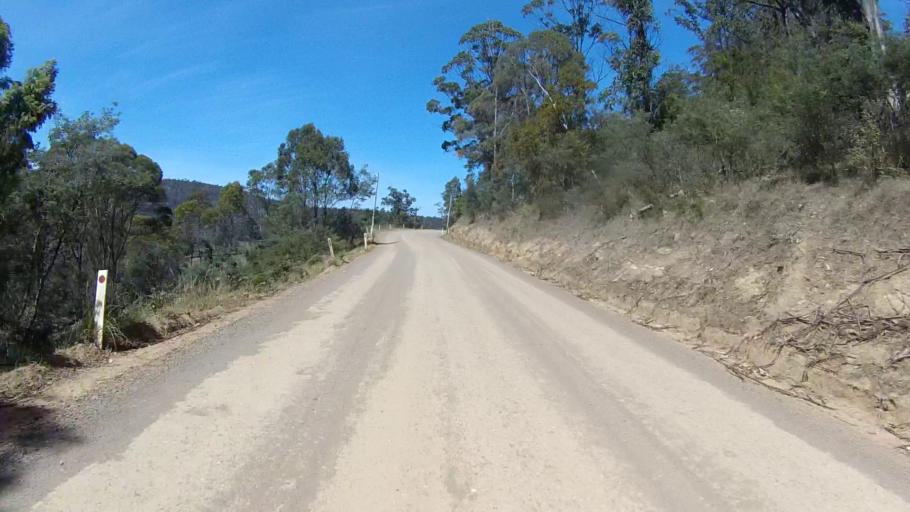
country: AU
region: Tasmania
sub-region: Sorell
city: Sorell
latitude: -42.7554
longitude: 147.6829
